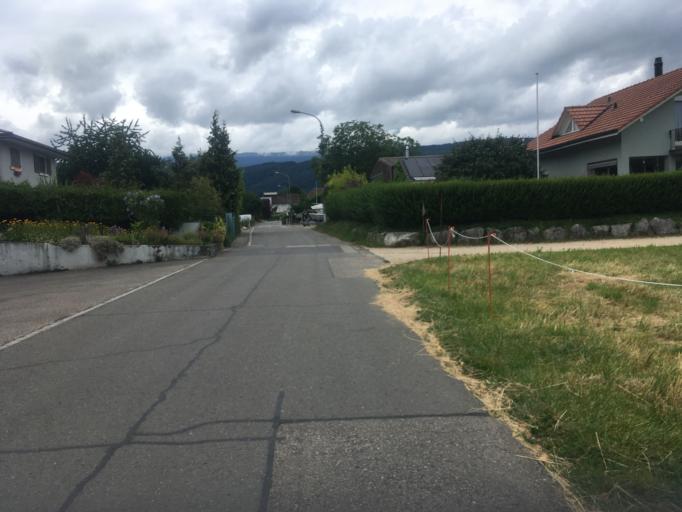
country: CH
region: Bern
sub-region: Seeland District
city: Erlach
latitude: 47.0431
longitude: 7.1002
